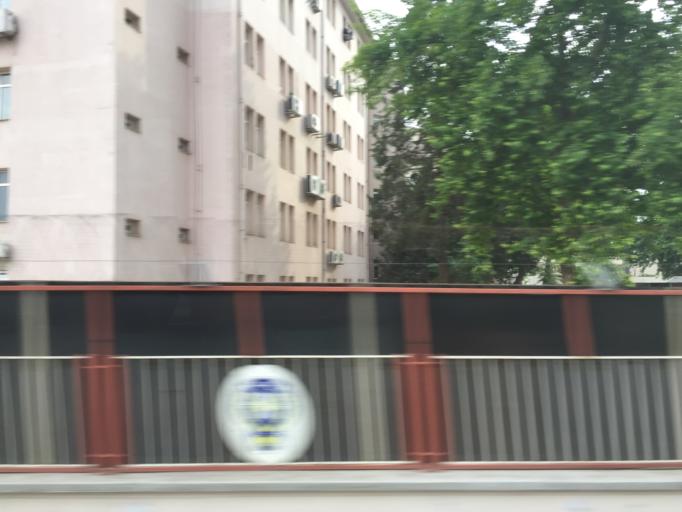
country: TR
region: Gaziantep
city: Gaziantep
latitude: 37.0670
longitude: 37.3748
